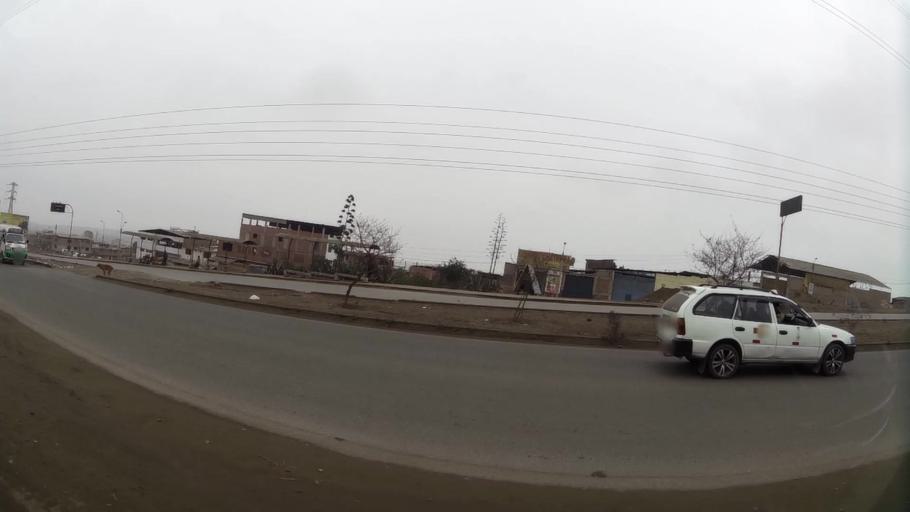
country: PE
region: Lima
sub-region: Lima
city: Surco
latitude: -12.2140
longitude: -76.9225
